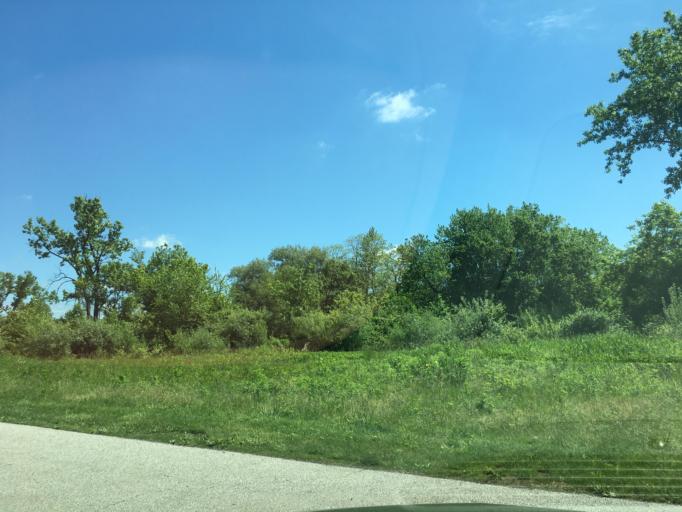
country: US
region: Ohio
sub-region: Cuyahoga County
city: Independence
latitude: 41.3927
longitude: -81.6303
